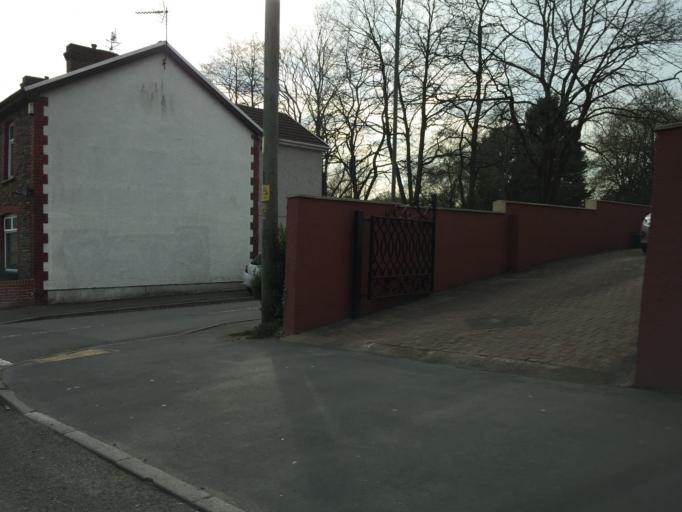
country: GB
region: Wales
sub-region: Caerphilly County Borough
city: Caerphilly
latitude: 51.5779
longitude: -3.2239
